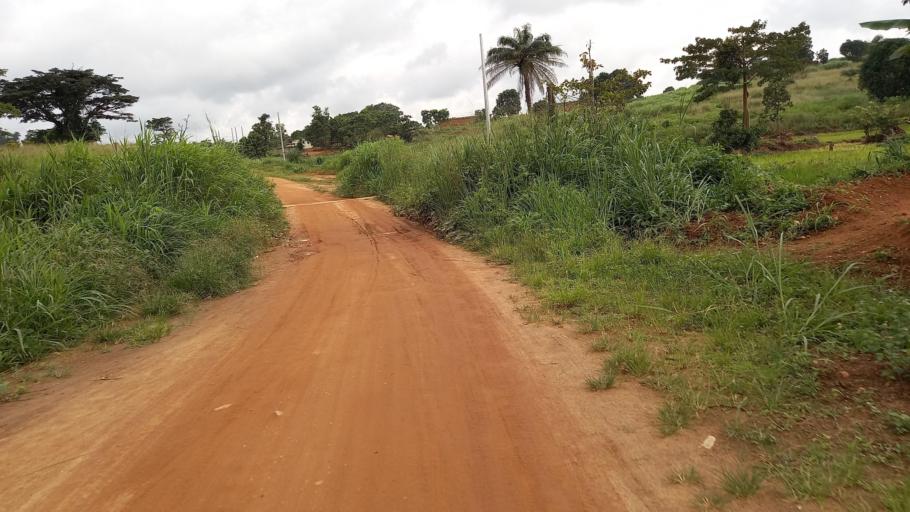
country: SL
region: Eastern Province
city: Kailahun
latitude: 8.2927
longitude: -10.5752
